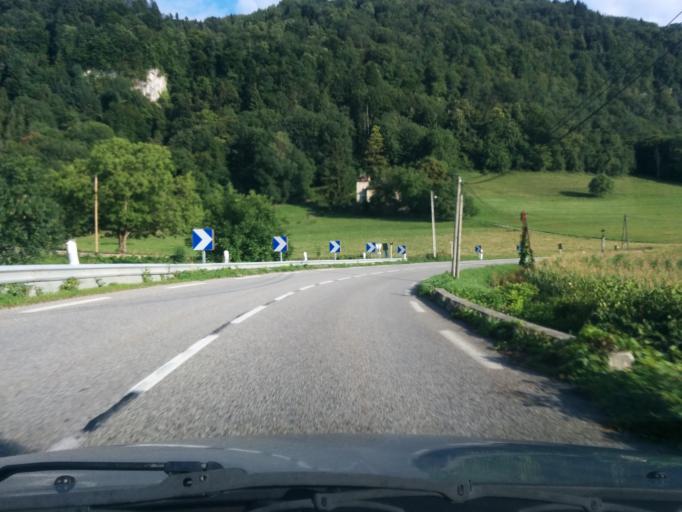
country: FR
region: Rhone-Alpes
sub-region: Departement de la Savoie
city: Saint-Beron
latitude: 45.4985
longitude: 5.7295
